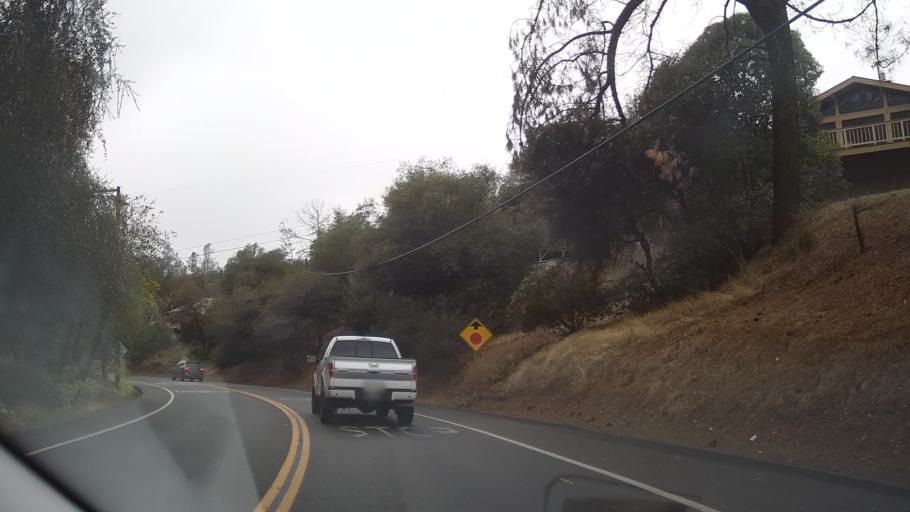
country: US
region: California
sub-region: Placer County
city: North Auburn
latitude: 38.9151
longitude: -121.0728
